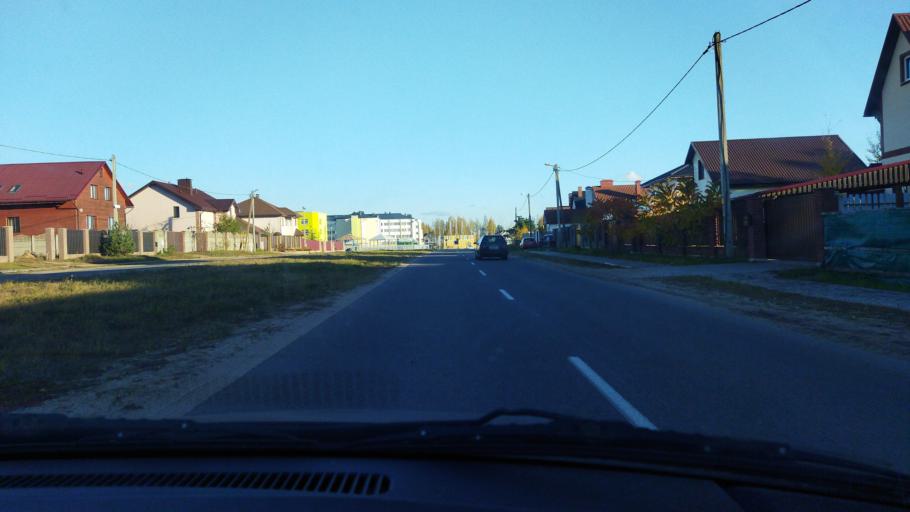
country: BY
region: Minsk
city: Kalodzishchy
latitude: 53.9131
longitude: 27.7682
